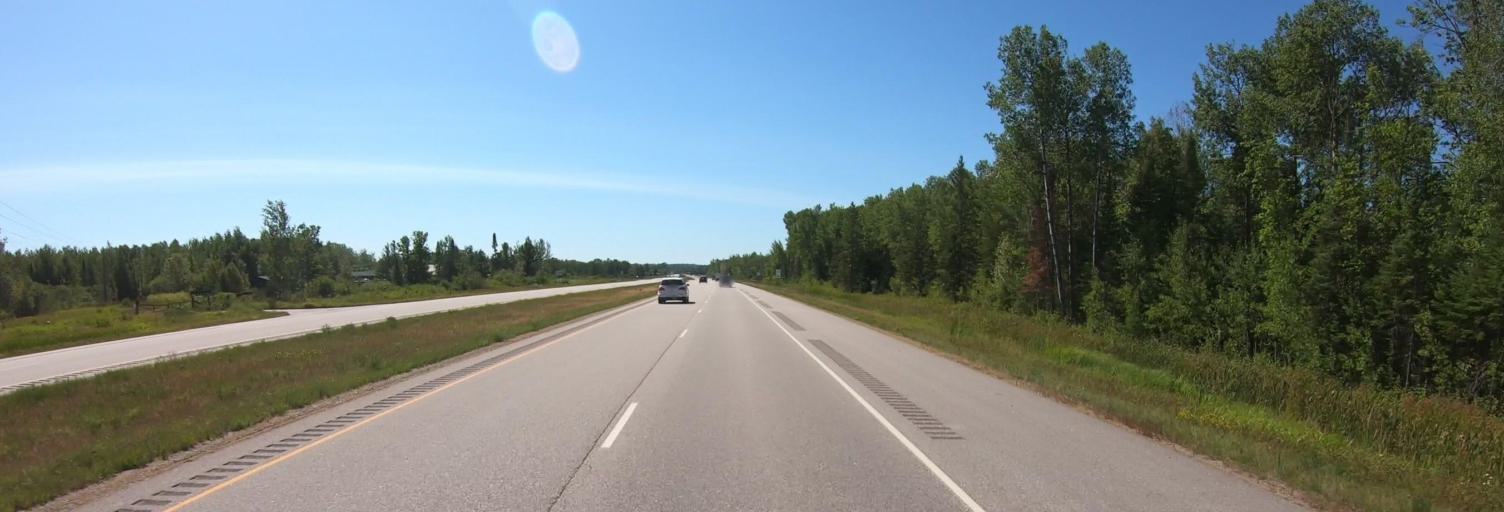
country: US
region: Minnesota
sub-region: Saint Louis County
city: Mountain Iron
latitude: 47.8199
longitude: -92.6748
